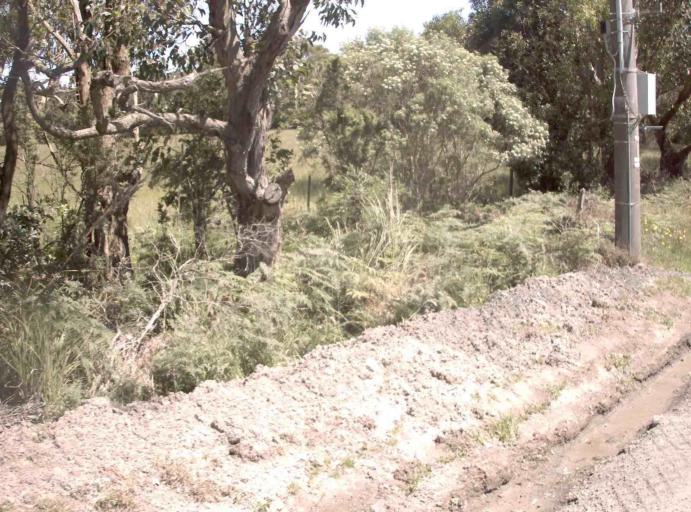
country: AU
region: Victoria
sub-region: Bass Coast
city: North Wonthaggi
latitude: -38.7651
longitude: 146.0634
